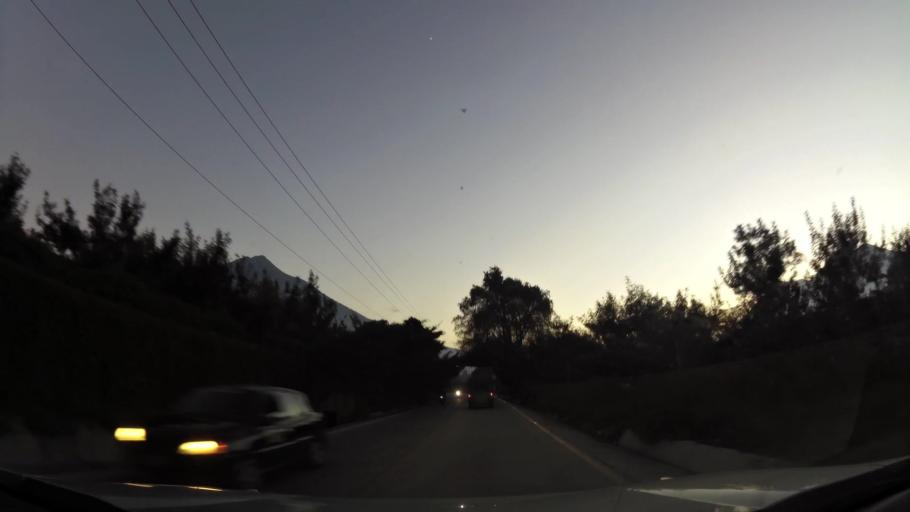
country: GT
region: Sacatepequez
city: Ciudad Vieja
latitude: 14.5376
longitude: -90.7483
